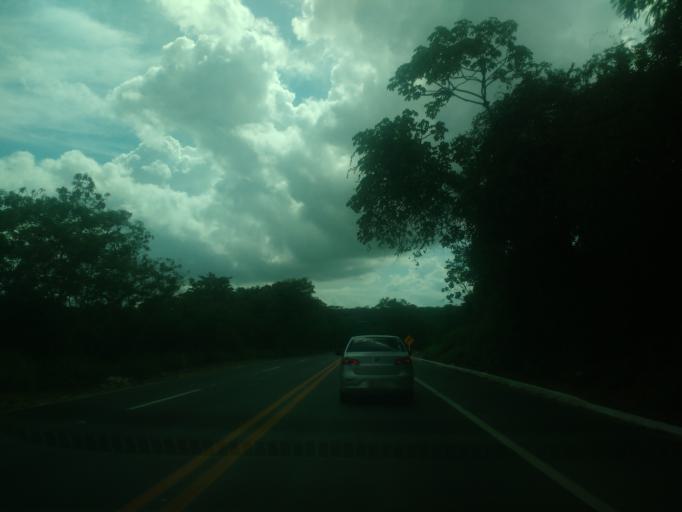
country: BR
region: Alagoas
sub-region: Marechal Deodoro
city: Marechal Deodoro
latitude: -9.6860
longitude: -35.8229
